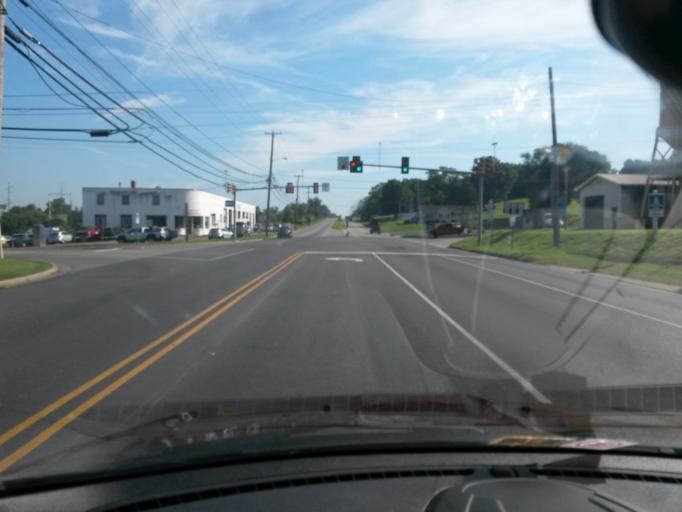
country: US
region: Virginia
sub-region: Rockingham County
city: Broadway
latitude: 38.6133
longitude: -78.7867
